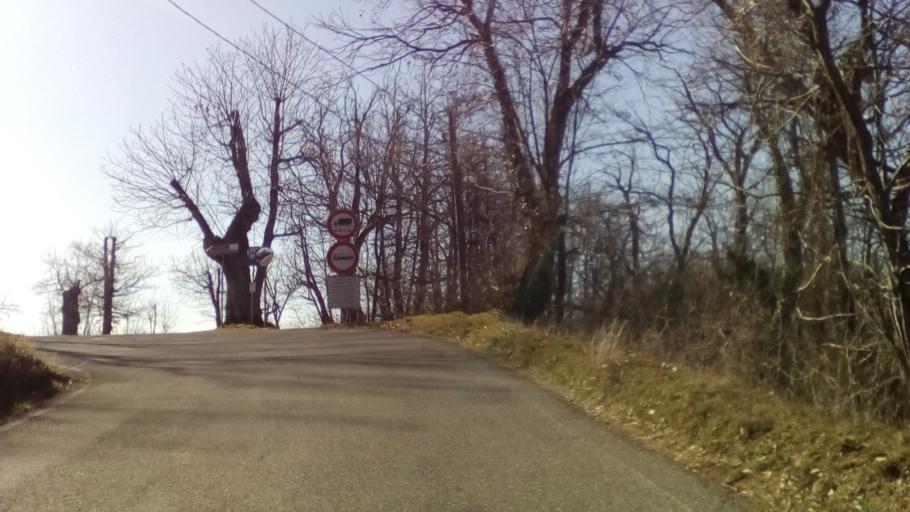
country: IT
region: Tuscany
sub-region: Provincia di Lucca
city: Castiglione di Garfagnana
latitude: 44.1468
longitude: 10.4387
